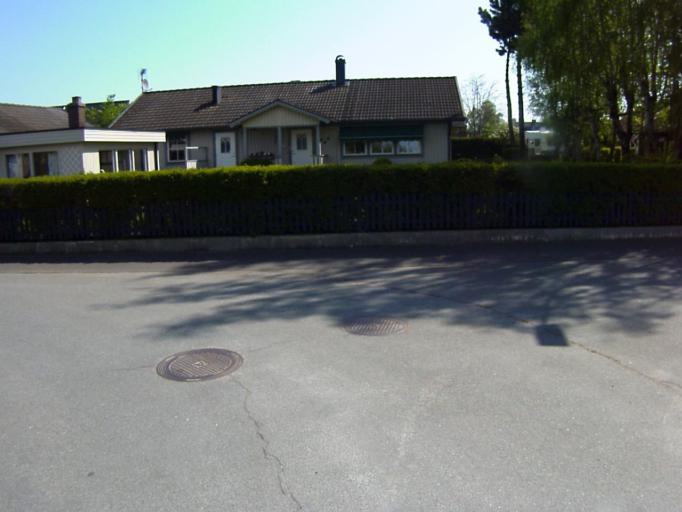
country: SE
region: Skane
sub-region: Kristianstads Kommun
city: Ahus
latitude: 55.9804
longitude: 14.2706
